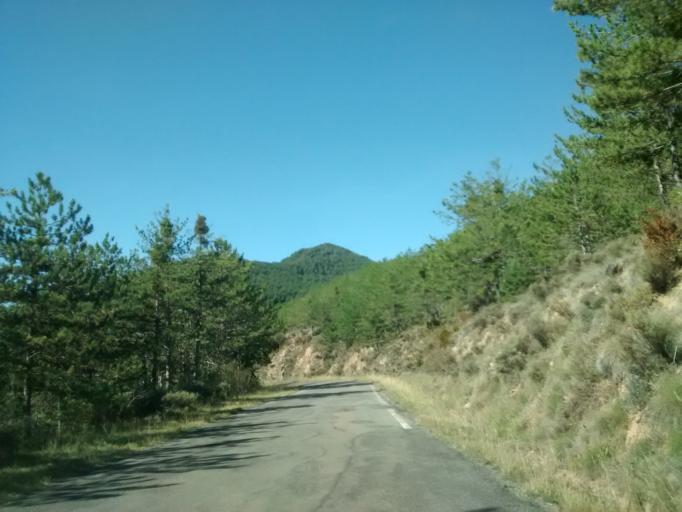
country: ES
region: Aragon
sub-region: Provincia de Huesca
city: Jaca
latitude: 42.4971
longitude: -0.5554
